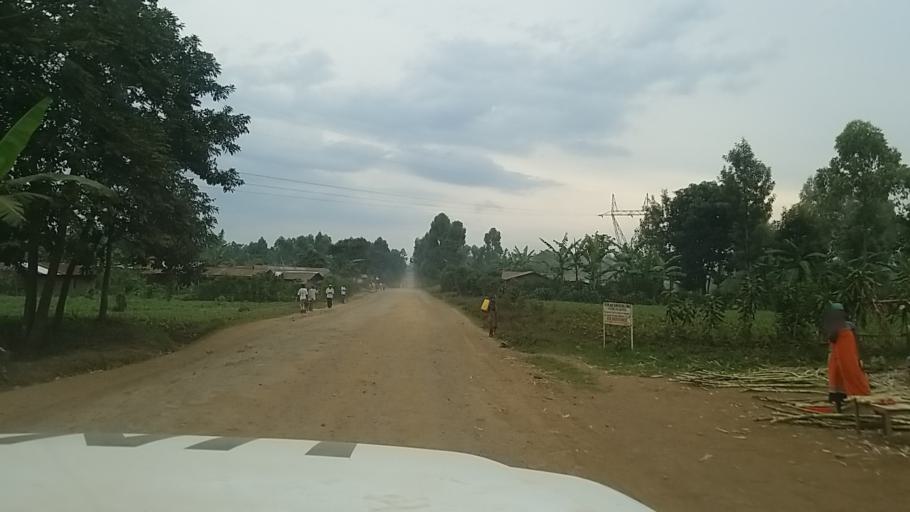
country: CD
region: South Kivu
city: Bukavu
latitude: -2.2688
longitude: 28.8194
